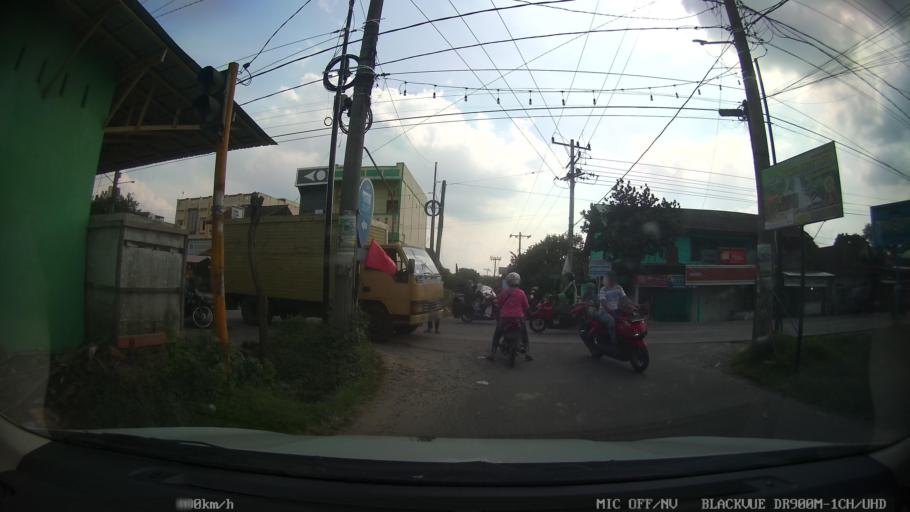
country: ID
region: North Sumatra
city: Binjai
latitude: 3.6346
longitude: 98.4893
